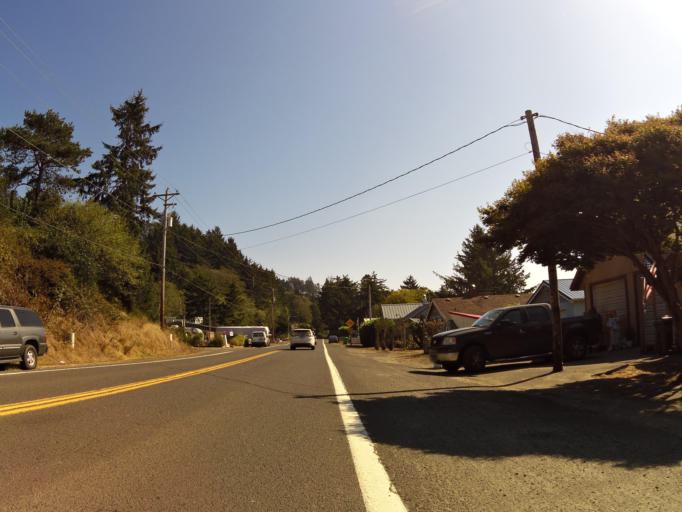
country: US
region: Oregon
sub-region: Tillamook County
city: Pacific City
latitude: 45.1970
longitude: -123.9584
